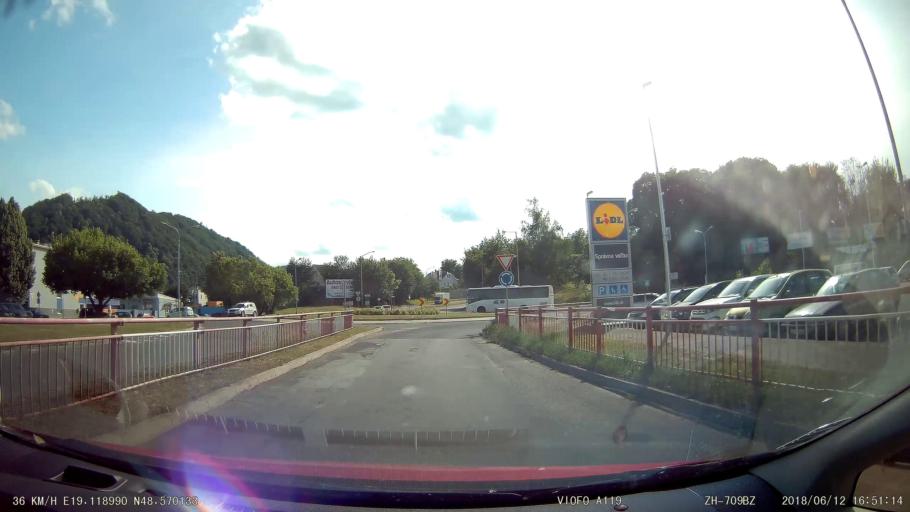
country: SK
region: Banskobystricky
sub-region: Okres Banska Bystrica
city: Zvolen
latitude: 48.5700
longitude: 19.1188
